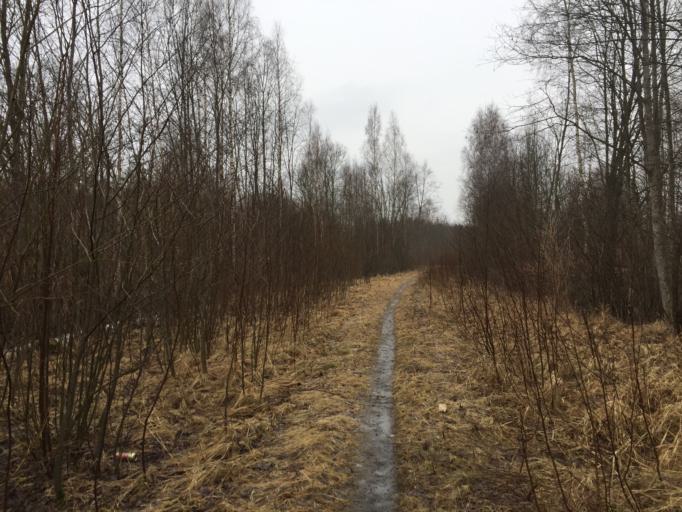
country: LV
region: Lielvarde
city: Lielvarde
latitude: 56.7276
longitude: 24.7785
